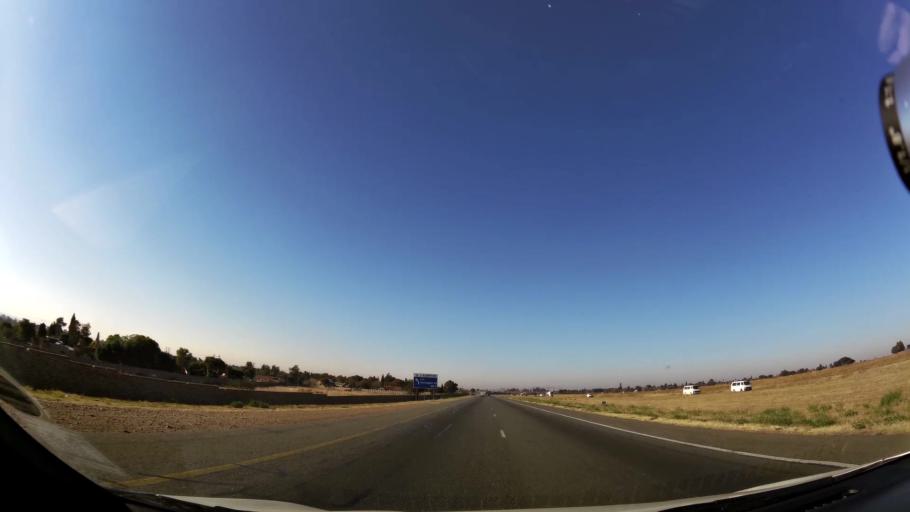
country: ZA
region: Gauteng
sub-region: Ekurhuleni Metropolitan Municipality
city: Germiston
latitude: -26.2963
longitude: 28.1073
